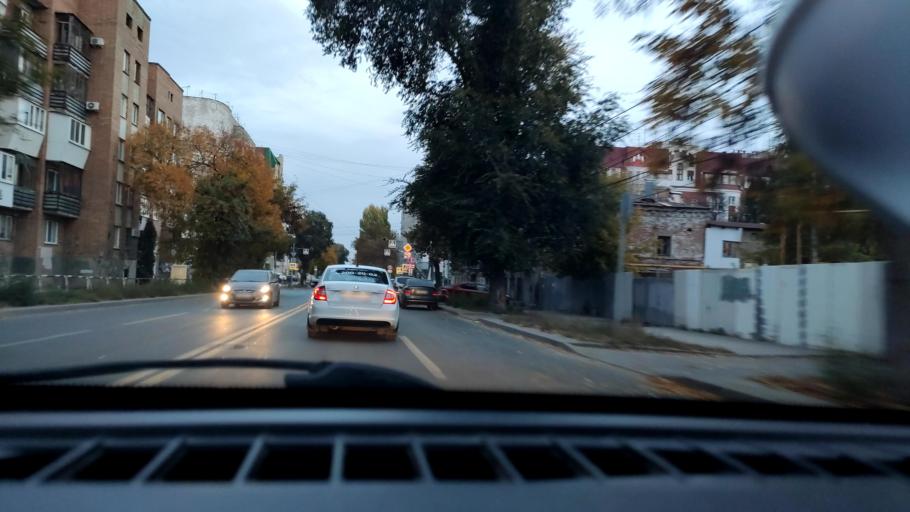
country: RU
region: Samara
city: Samara
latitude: 53.1832
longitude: 50.0972
